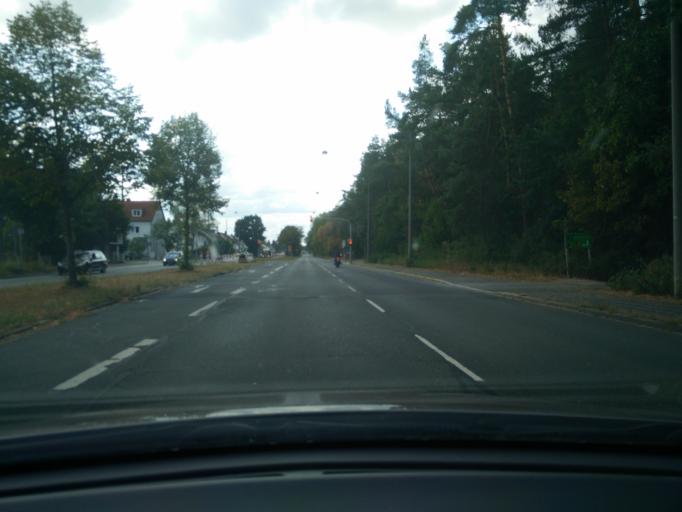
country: DE
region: Bavaria
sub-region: Regierungsbezirk Mittelfranken
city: Nuernberg
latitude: 49.4082
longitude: 11.1014
